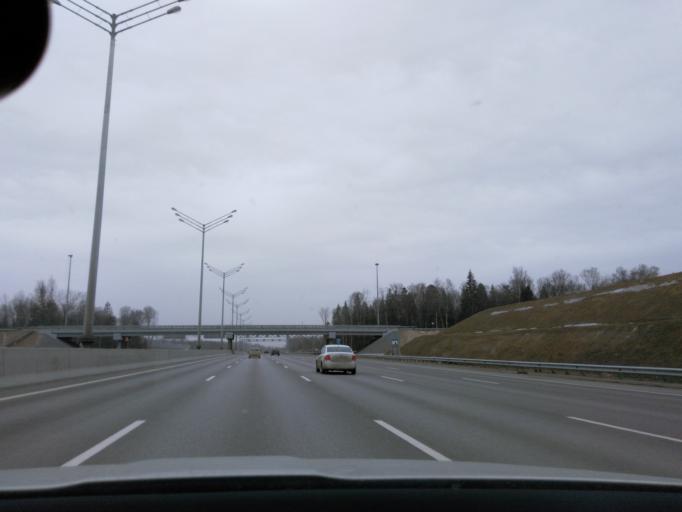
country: RU
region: Moscow
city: Khimki
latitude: 55.9504
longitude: 37.4357
